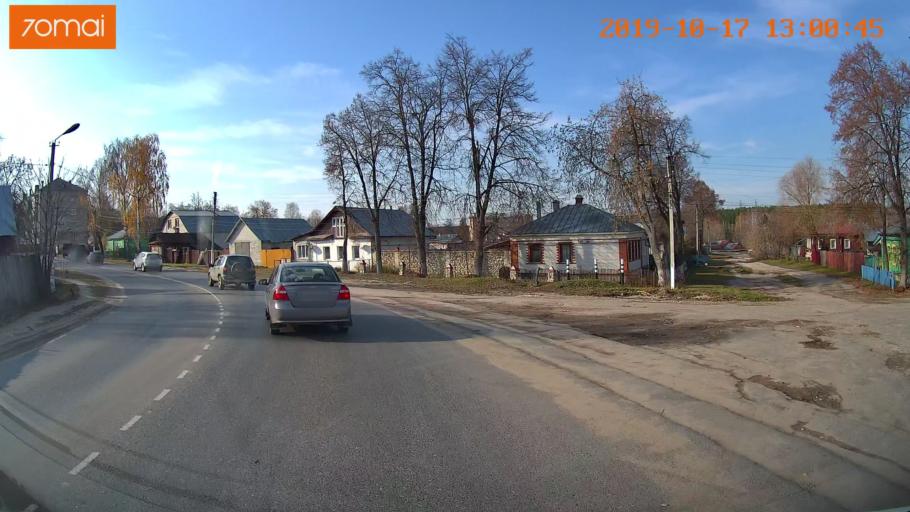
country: RU
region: Rjazan
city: Kasimov
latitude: 54.9451
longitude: 41.3755
